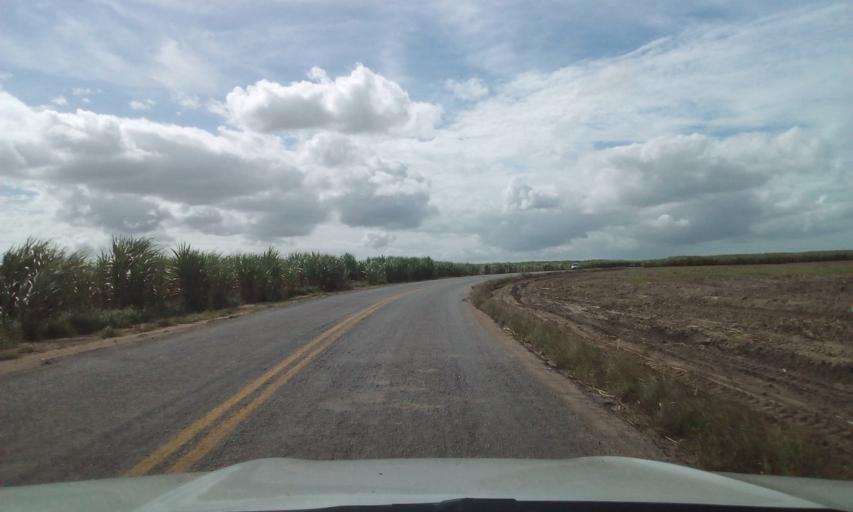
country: BR
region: Paraiba
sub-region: Santa Rita
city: Santa Rita
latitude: -7.0699
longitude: -34.9888
